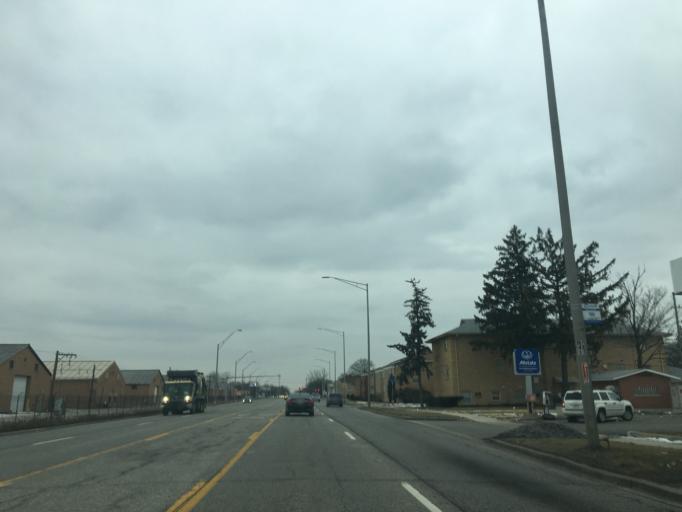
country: US
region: Illinois
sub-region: Cook County
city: North Riverside
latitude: 41.8498
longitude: -87.8375
